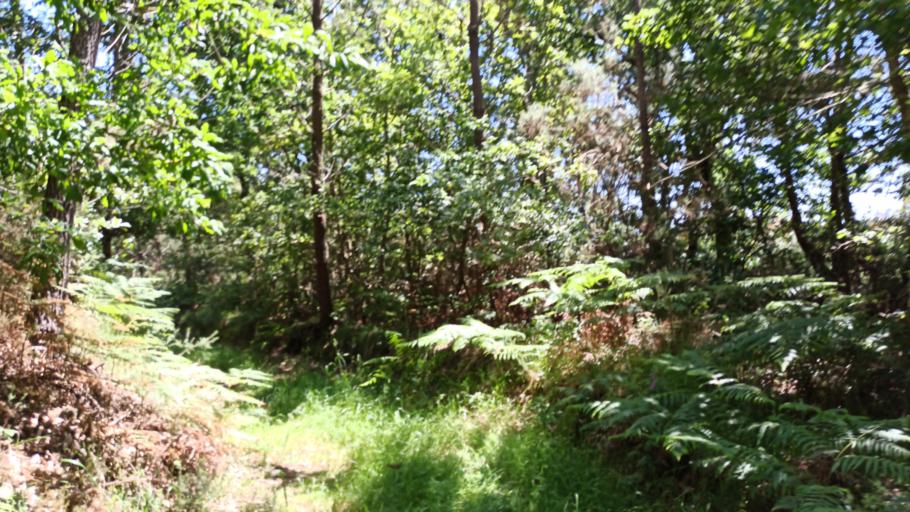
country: ES
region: Galicia
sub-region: Provincia da Coruna
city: Negreira
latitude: 42.9179
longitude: -8.7197
